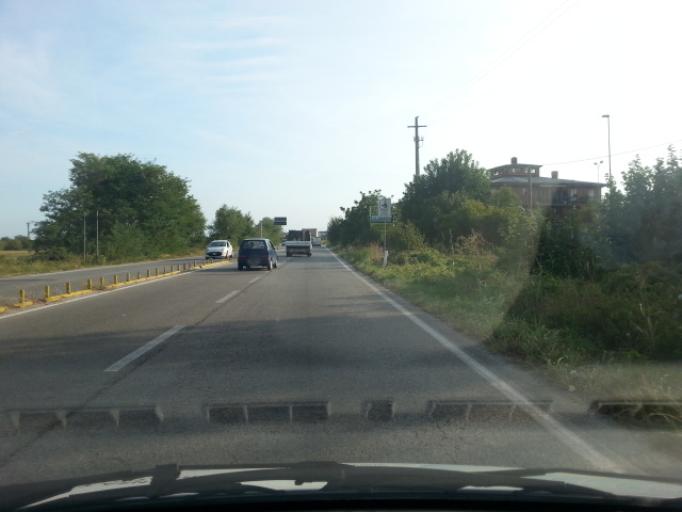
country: IT
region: Piedmont
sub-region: Provincia di Torino
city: Gerbole
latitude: 45.0089
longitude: 7.5199
